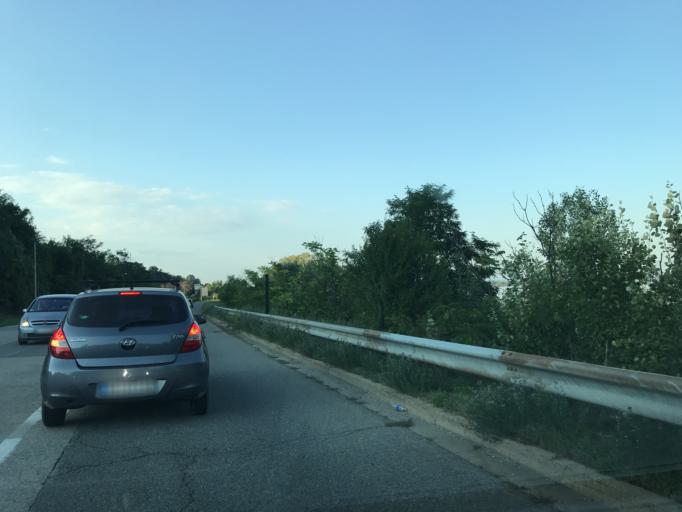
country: RO
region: Mehedinti
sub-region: Comuna Gogosu
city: Ostrovu Mare
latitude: 44.4736
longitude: 22.4497
